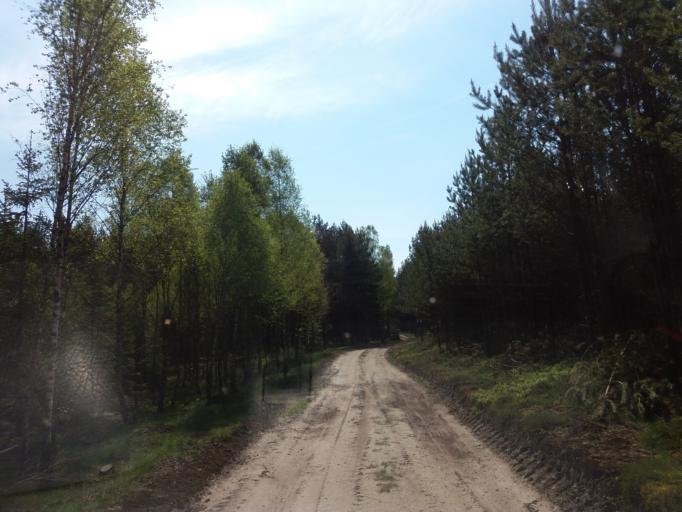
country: PL
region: West Pomeranian Voivodeship
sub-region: Powiat choszczenski
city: Bierzwnik
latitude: 53.0968
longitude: 15.7250
